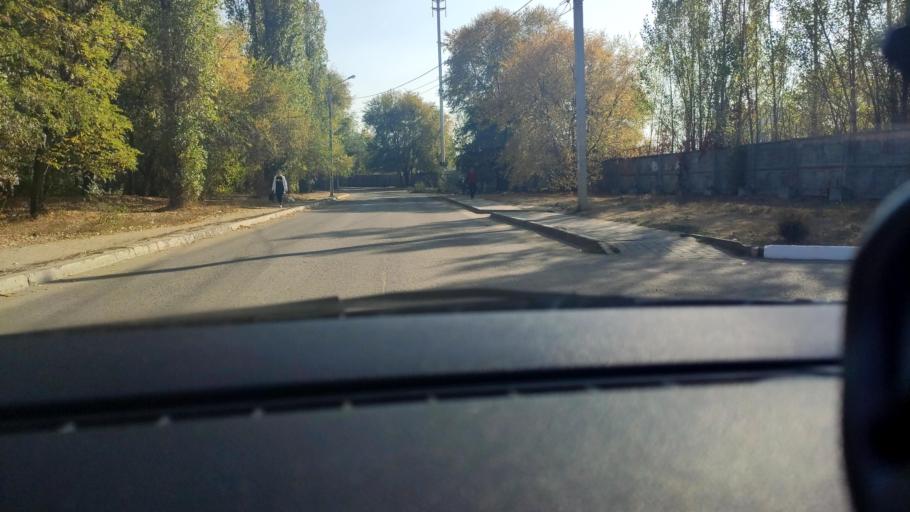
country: RU
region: Voronezj
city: Pridonskoy
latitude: 51.6247
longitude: 39.0686
